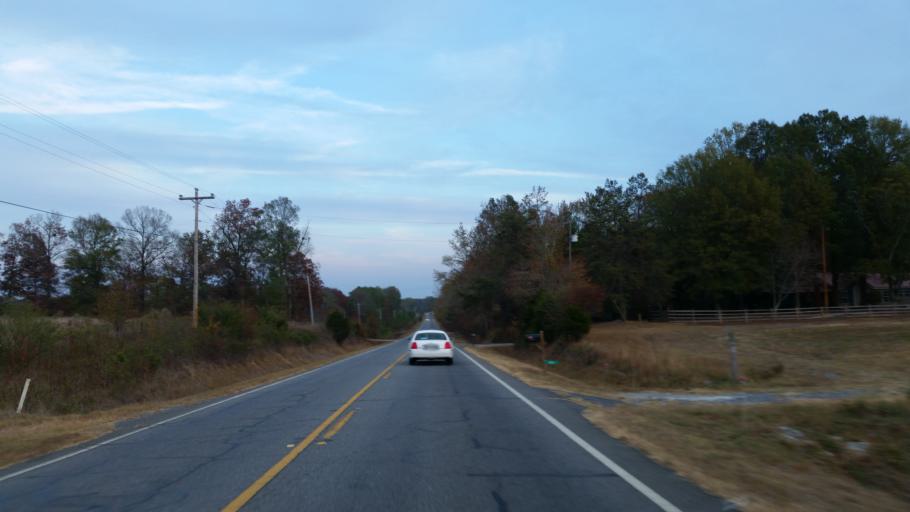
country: US
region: Georgia
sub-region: Gordon County
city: Calhoun
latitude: 34.6041
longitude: -84.8329
